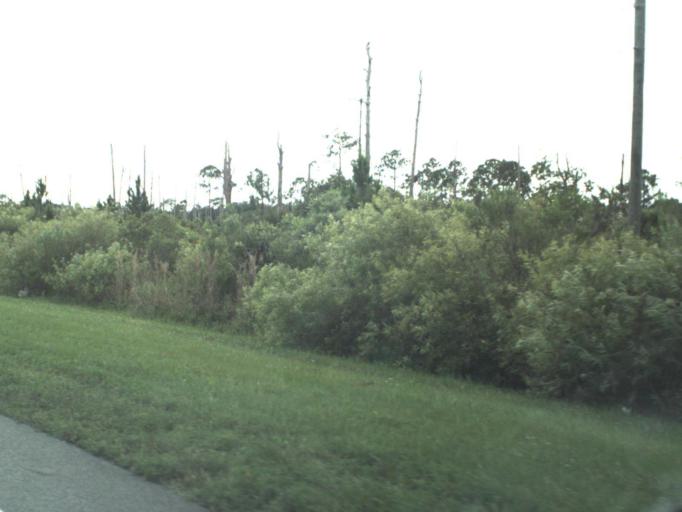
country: US
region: Florida
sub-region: Brevard County
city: Cocoa West
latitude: 28.3835
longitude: -80.7908
